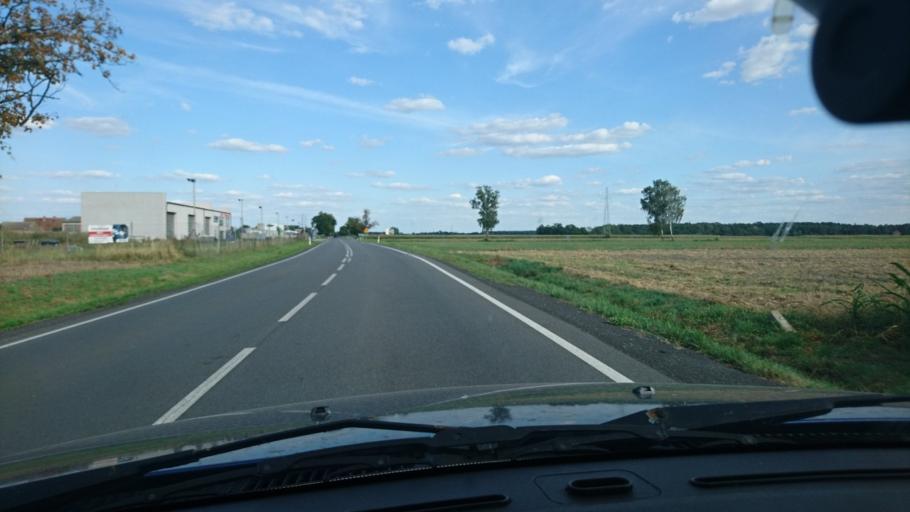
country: PL
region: Greater Poland Voivodeship
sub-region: Powiat krotoszynski
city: Zduny
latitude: 51.7220
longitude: 17.3483
